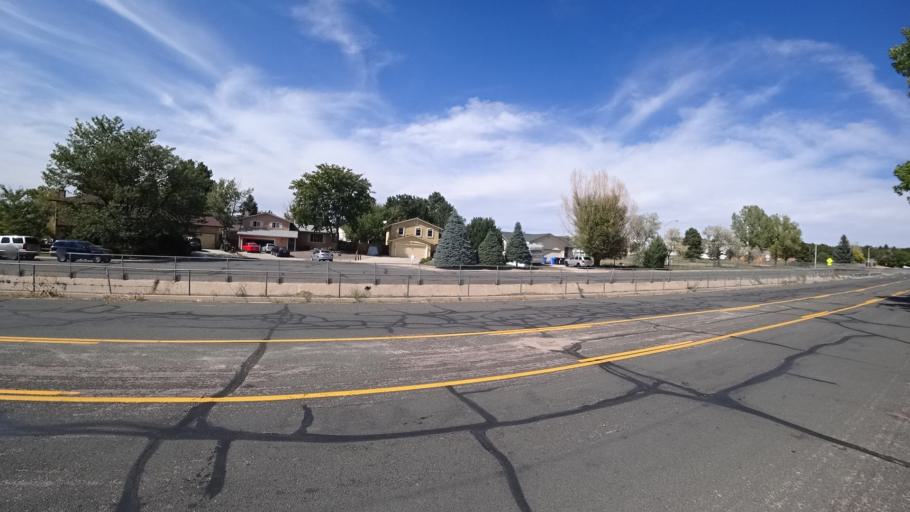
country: US
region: Colorado
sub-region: El Paso County
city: Cimarron Hills
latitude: 38.9013
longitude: -104.7572
